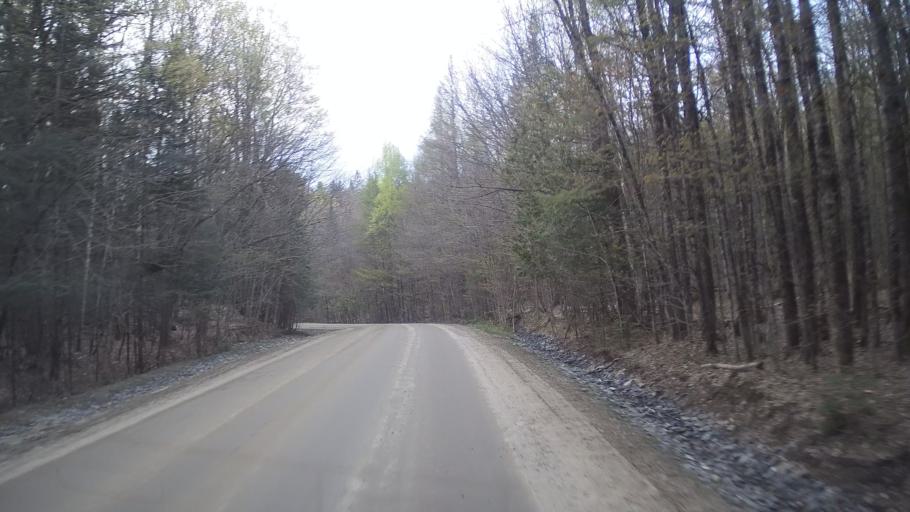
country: US
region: Vermont
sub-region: Caledonia County
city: Lyndonville
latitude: 44.5995
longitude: -71.9599
